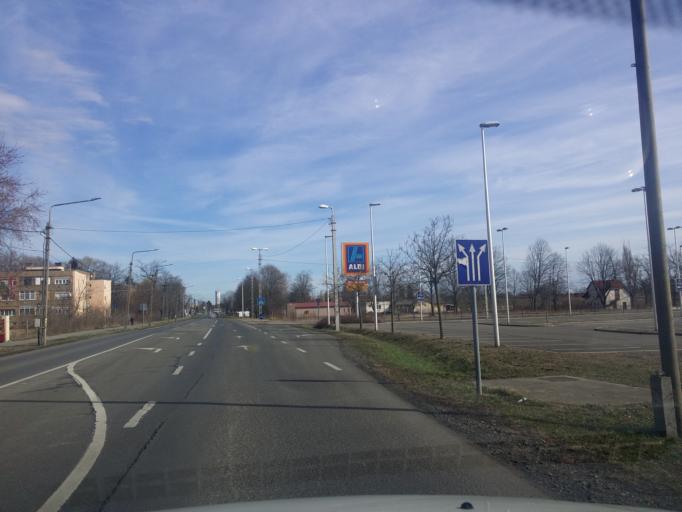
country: HU
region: Baranya
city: Mohacs
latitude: 45.9973
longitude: 18.6623
